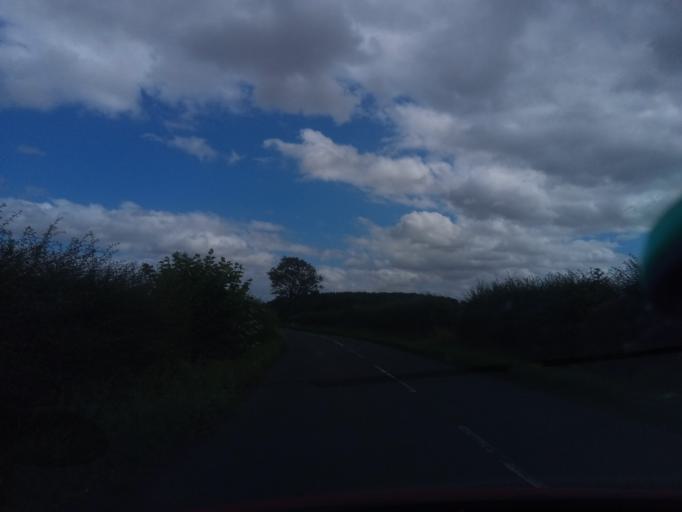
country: GB
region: Scotland
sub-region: The Scottish Borders
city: Coldstream
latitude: 55.6329
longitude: -2.3347
